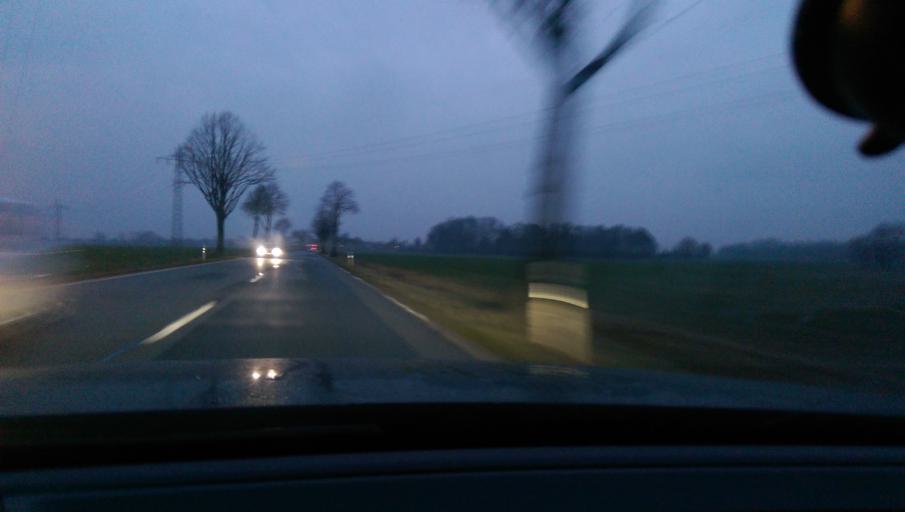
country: DE
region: Lower Saxony
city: Grossgoltern
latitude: 52.3486
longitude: 9.5490
